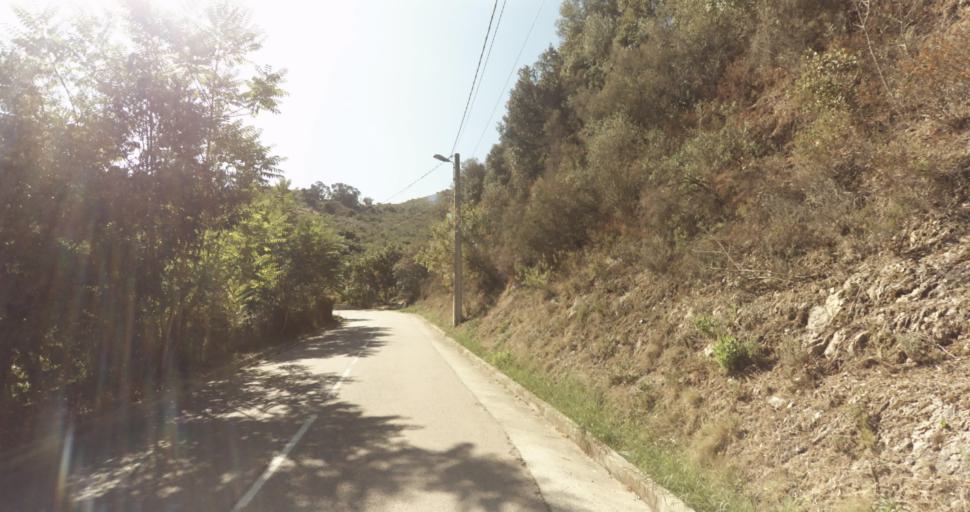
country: FR
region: Corsica
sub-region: Departement de la Corse-du-Sud
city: Ajaccio
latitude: 41.9270
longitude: 8.7066
